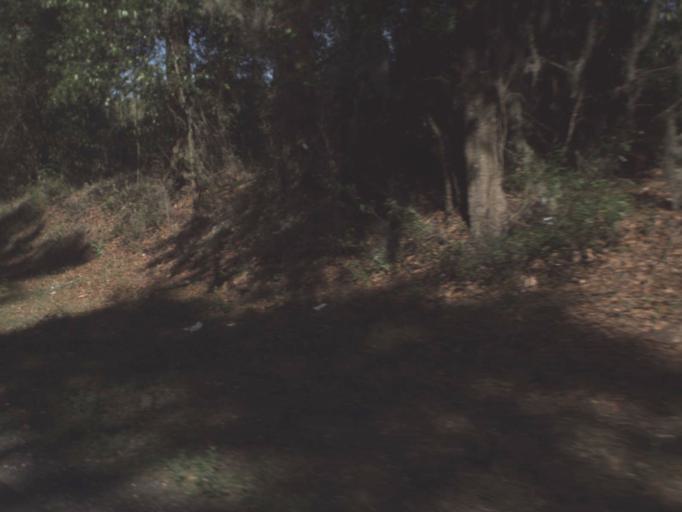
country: US
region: Florida
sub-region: Marion County
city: Dunnellon
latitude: 29.1175
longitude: -82.4394
